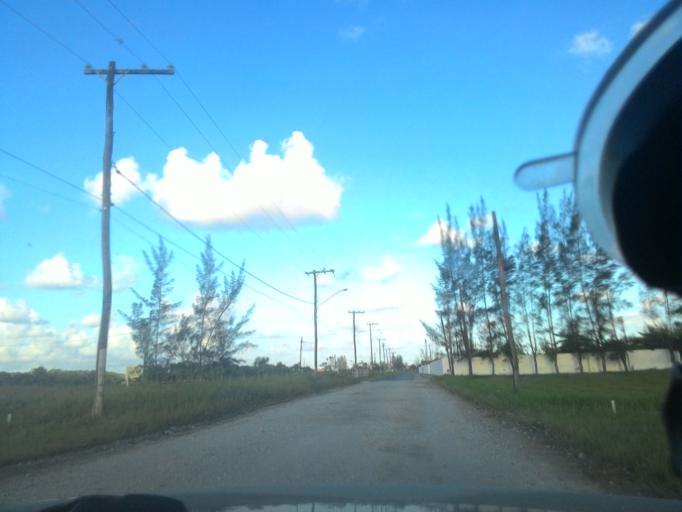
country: BR
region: Sao Paulo
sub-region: Iguape
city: Iguape
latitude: -24.8269
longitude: -47.6680
